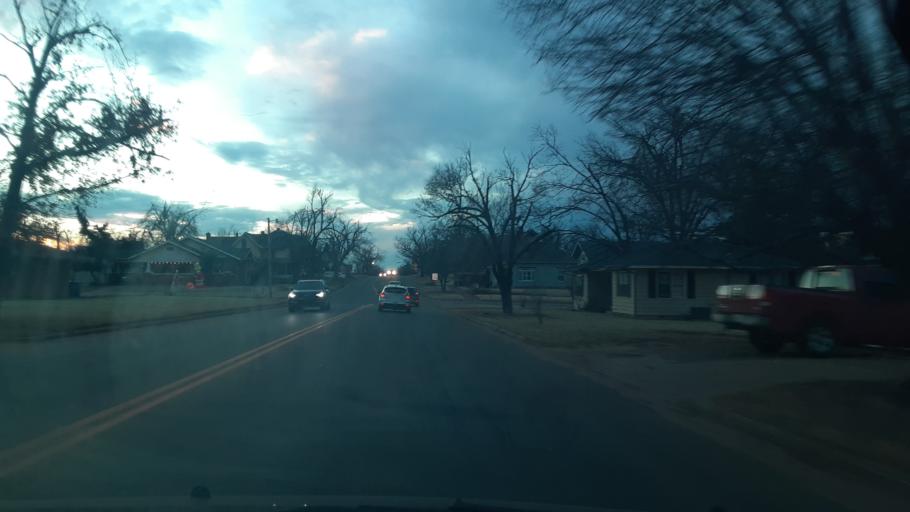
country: US
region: Oklahoma
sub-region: Logan County
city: Guthrie
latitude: 35.8802
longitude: -97.4142
